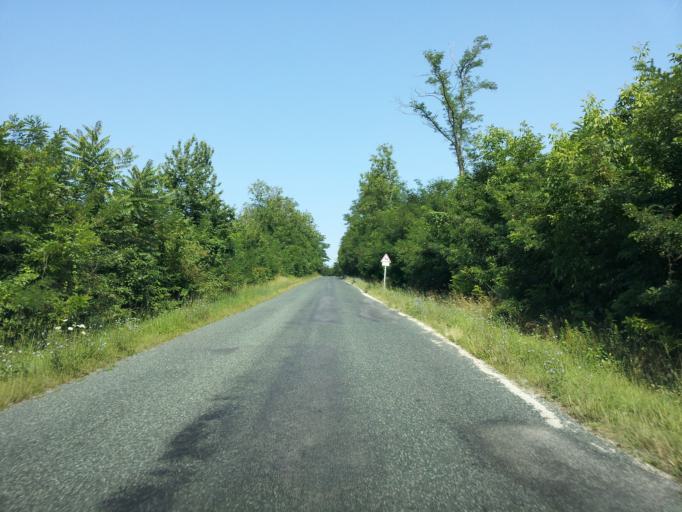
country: HU
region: Zala
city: Heviz
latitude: 46.8663
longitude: 17.1537
